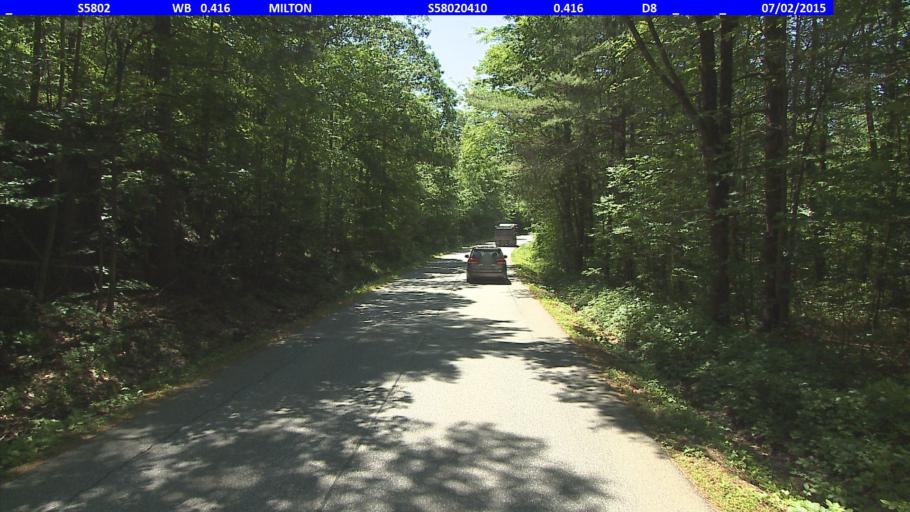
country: US
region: Vermont
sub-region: Chittenden County
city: Colchester
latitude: 44.6141
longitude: -73.2038
